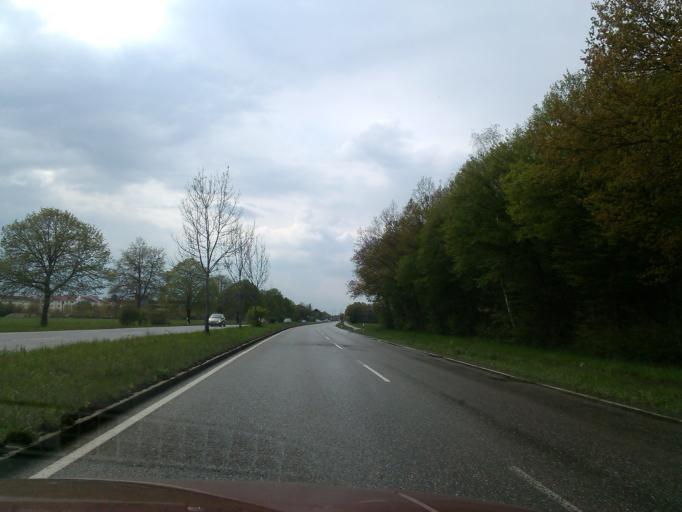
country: DE
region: Bavaria
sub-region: Upper Bavaria
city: Neuried
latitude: 48.1144
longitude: 11.4603
